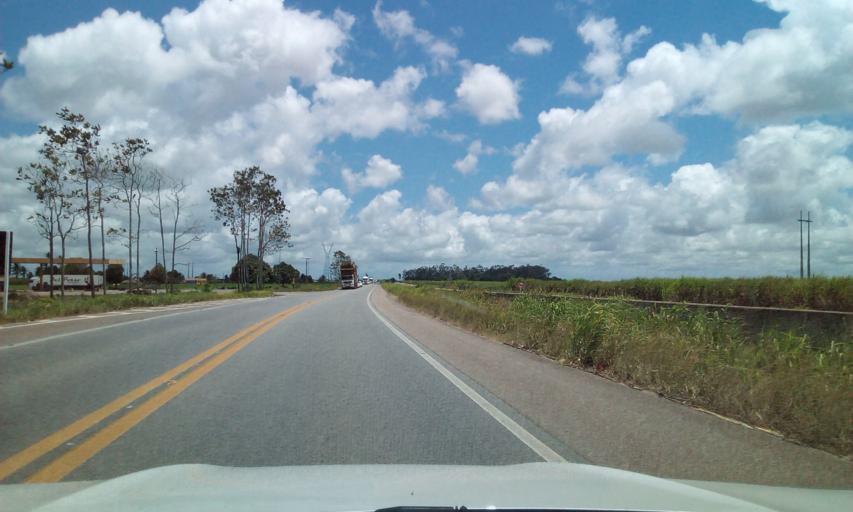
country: BR
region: Alagoas
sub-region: Campo Alegre
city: Campo Alegre
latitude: -9.9000
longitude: -36.2500
